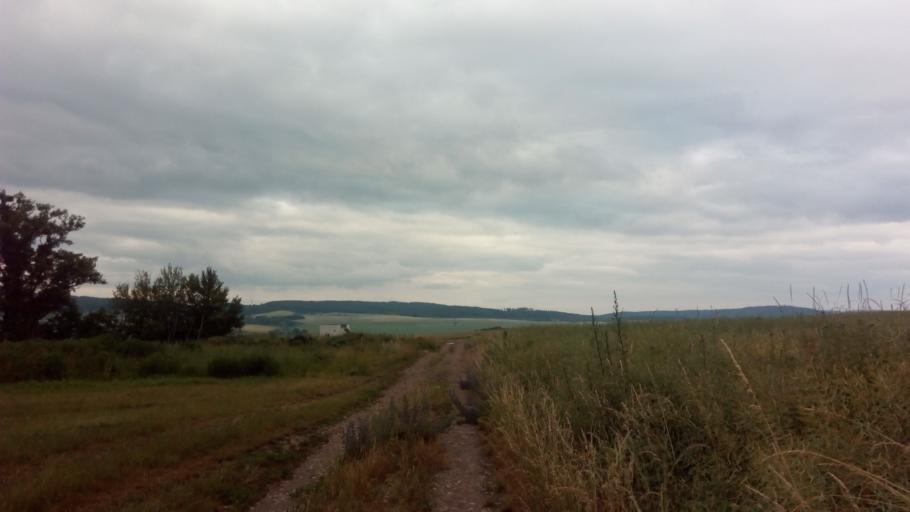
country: CZ
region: South Moravian
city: Ricany
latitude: 49.2101
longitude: 16.3874
